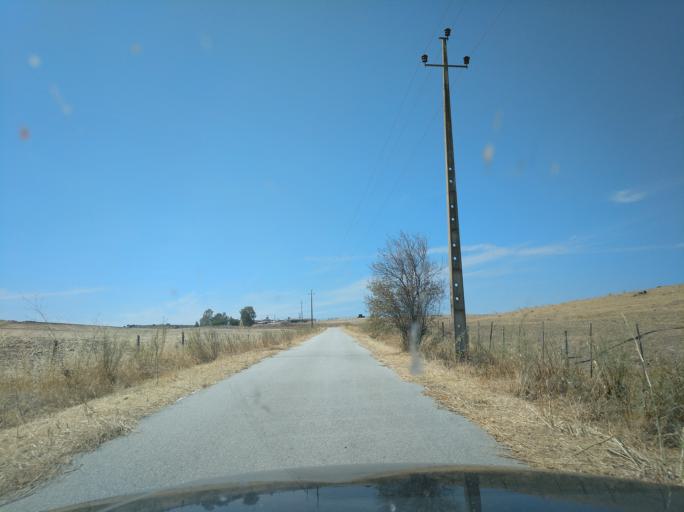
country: PT
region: Portalegre
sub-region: Campo Maior
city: Campo Maior
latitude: 38.9618
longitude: -7.1102
